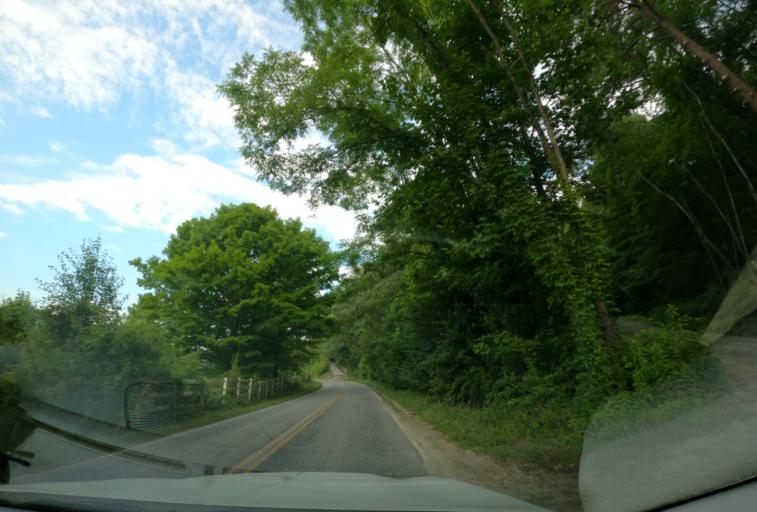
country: US
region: North Carolina
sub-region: Transylvania County
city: Brevard
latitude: 35.1857
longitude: -82.9165
